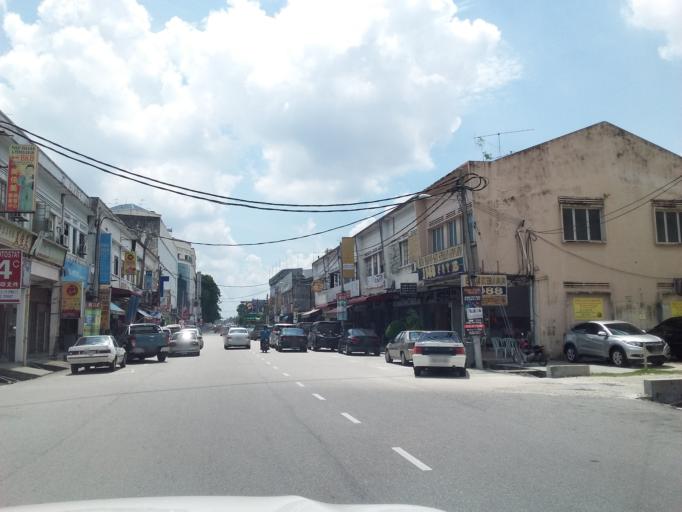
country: MY
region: Johor
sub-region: Daerah Batu Pahat
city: Batu Pahat
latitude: 1.8515
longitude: 102.9282
